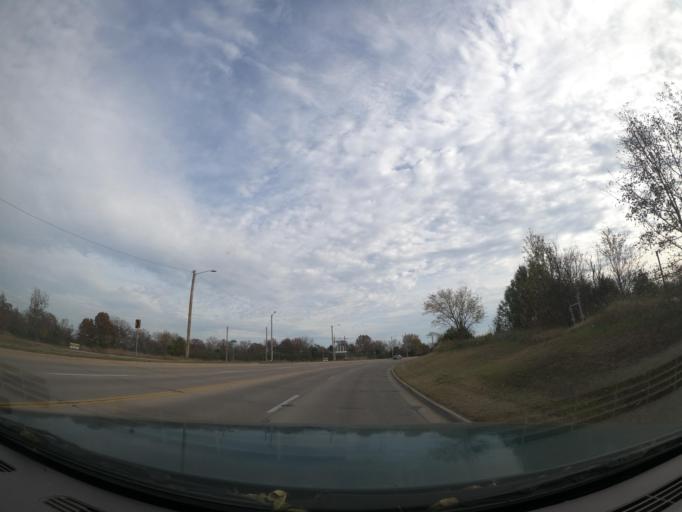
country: US
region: Oklahoma
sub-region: Tulsa County
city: Turley
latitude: 36.2107
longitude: -95.9944
